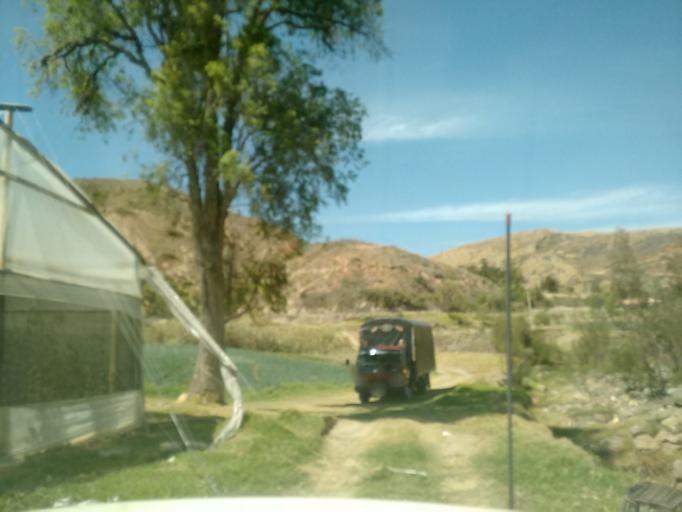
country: CO
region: Boyaca
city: Sachica
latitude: 5.5828
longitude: -73.5119
